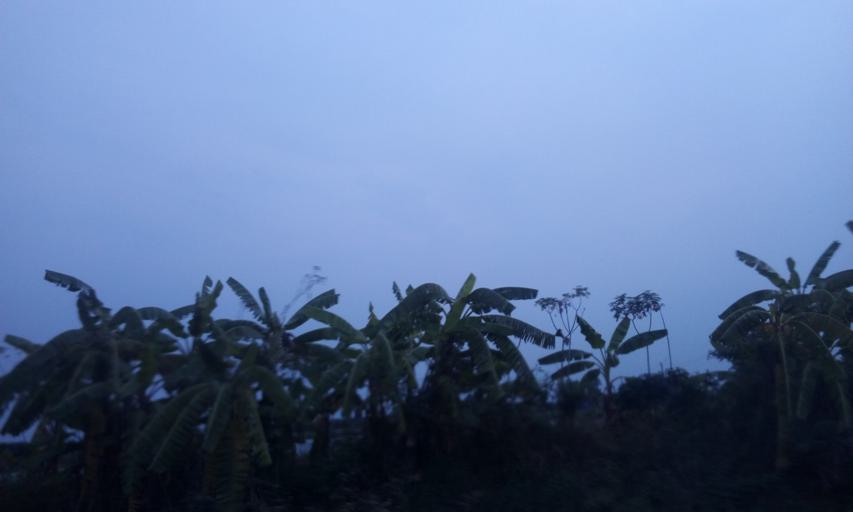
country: TH
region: Chachoengsao
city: Plaeng Yao
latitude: 13.5870
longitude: 101.2132
